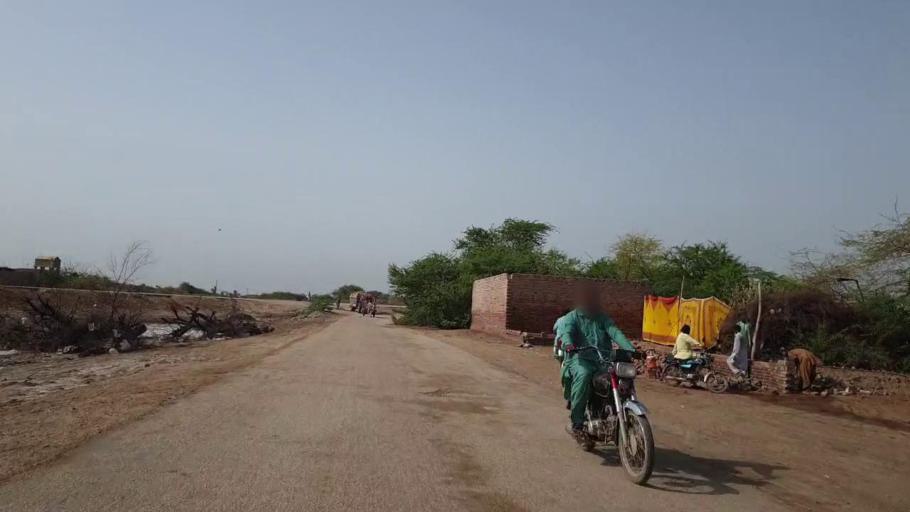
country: PK
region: Sindh
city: Jam Sahib
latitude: 26.2969
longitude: 68.6359
